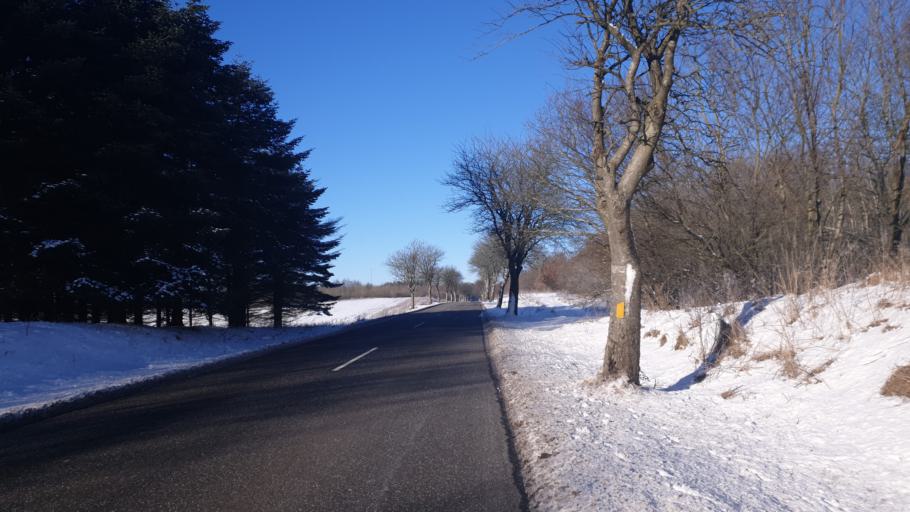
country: DK
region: Central Jutland
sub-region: Hedensted Kommune
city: Hedensted
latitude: 55.8014
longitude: 9.7195
